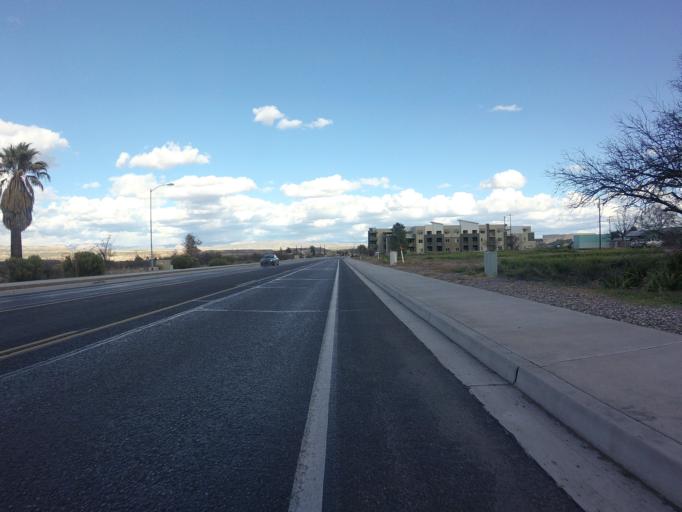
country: US
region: Arizona
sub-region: Yavapai County
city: Cottonwood
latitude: 34.7395
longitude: -112.0325
